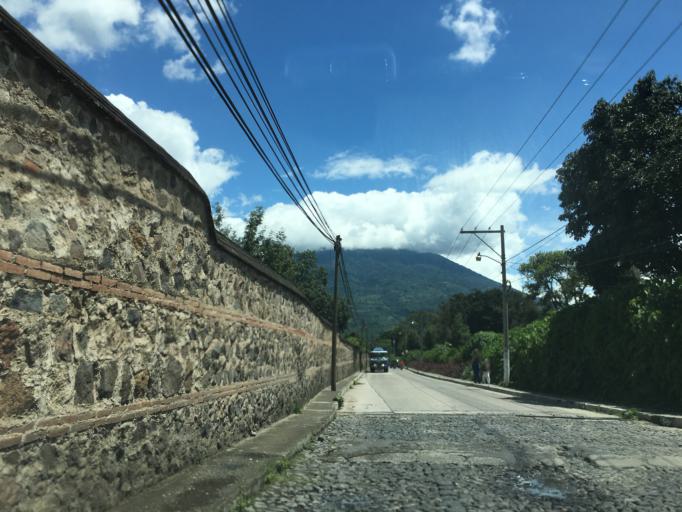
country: GT
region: Sacatepequez
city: Antigua Guatemala
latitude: 14.5485
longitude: -90.7286
